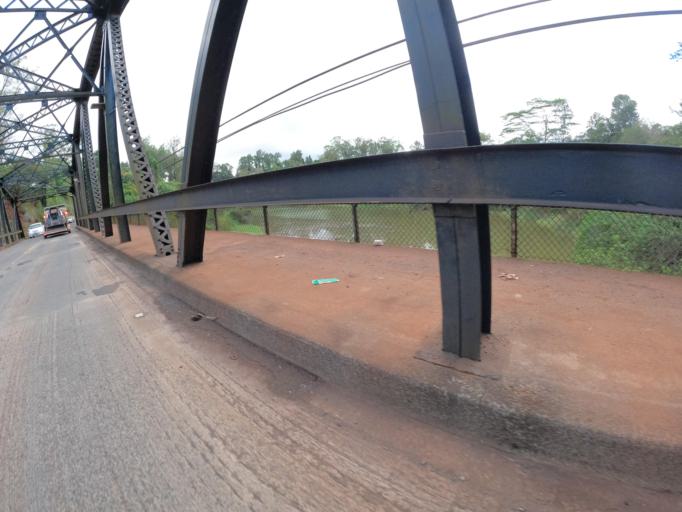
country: US
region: Hawaii
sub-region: Honolulu County
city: Wahiawa
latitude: 21.5009
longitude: -158.0296
